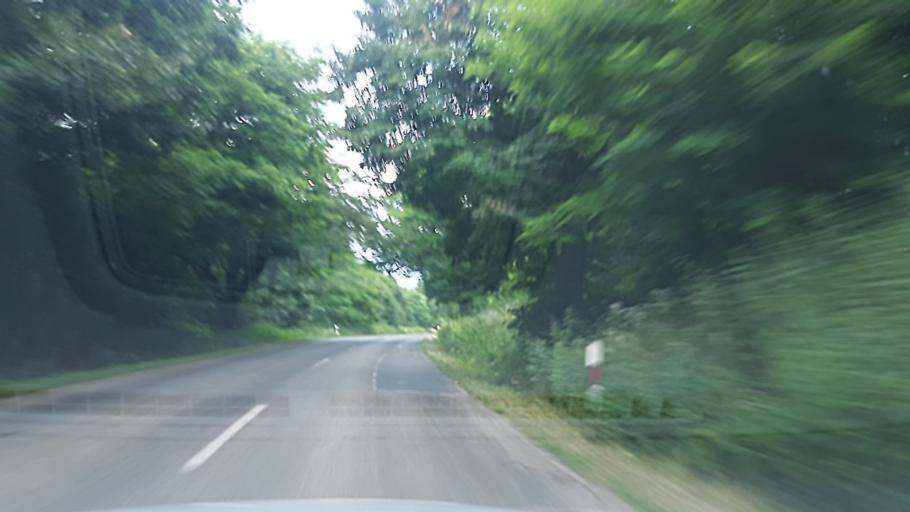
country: HU
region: Somogy
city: Kaposvar
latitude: 46.2611
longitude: 17.8268
